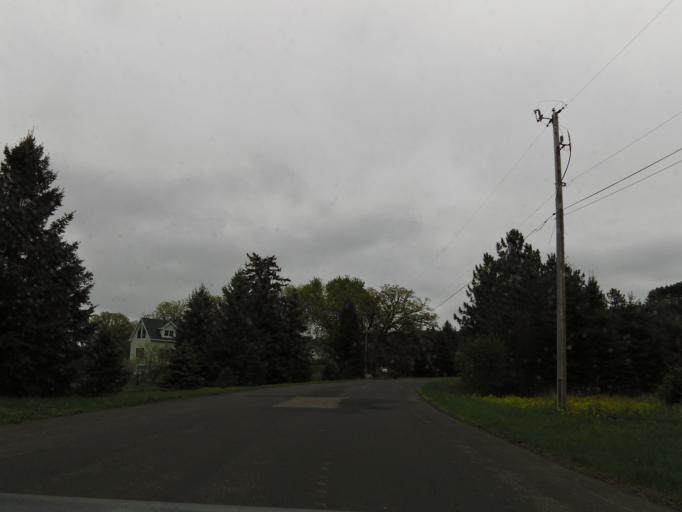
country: US
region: Minnesota
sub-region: Washington County
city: Lake Elmo
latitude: 44.9802
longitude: -92.8328
